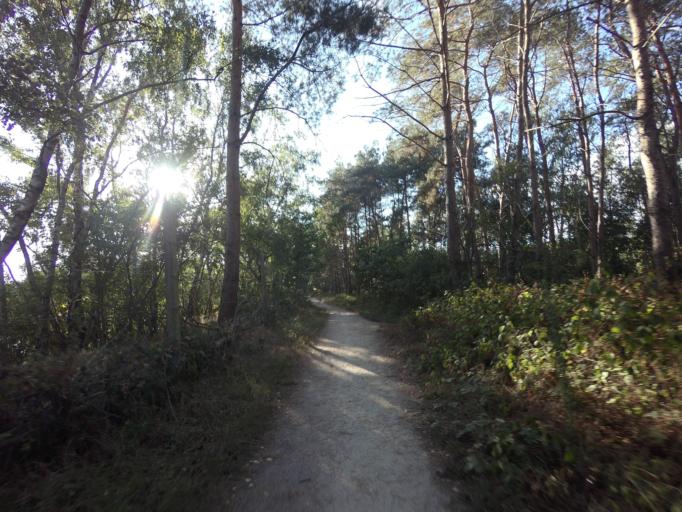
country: NL
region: North Brabant
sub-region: Gemeente Mill en Sint Hubert
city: Wilbertoord
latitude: 51.6931
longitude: 5.7470
